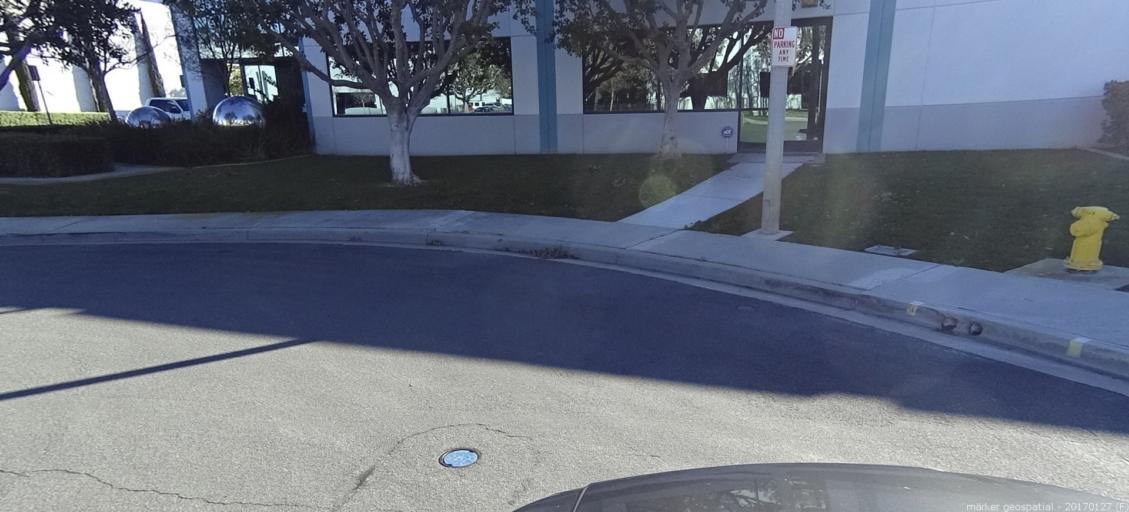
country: US
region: California
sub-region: Orange County
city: Foothill Ranch
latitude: 33.6663
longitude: -117.6581
